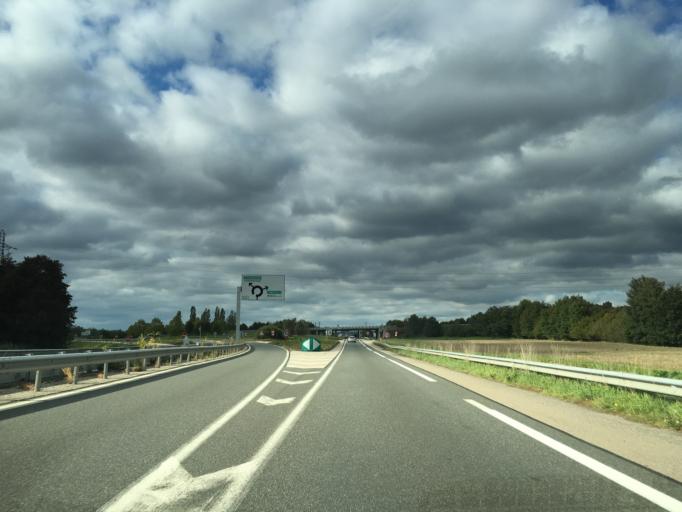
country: FR
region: Lorraine
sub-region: Departement de Meurthe-et-Moselle
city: Chanteheux
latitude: 48.5656
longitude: 6.5397
